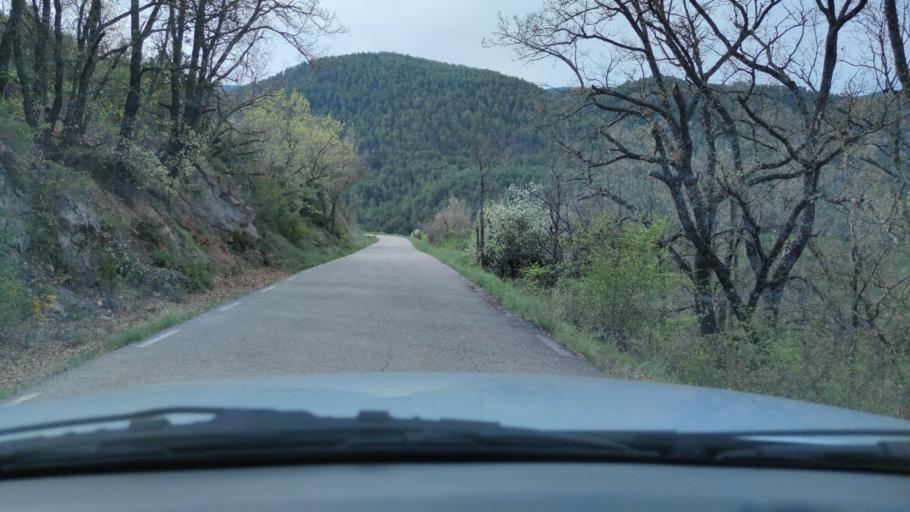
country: ES
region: Catalonia
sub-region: Provincia de Lleida
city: Alas i Cerc
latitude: 42.2338
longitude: 1.4763
